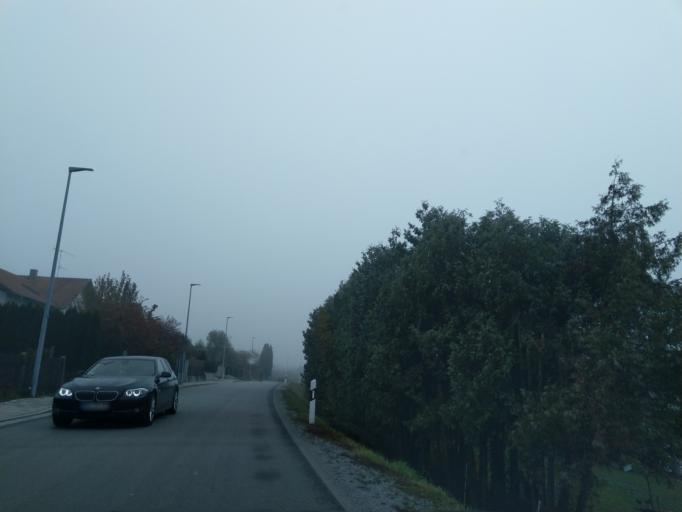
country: DE
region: Bavaria
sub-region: Lower Bavaria
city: Hengersberg
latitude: 48.7727
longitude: 13.0607
